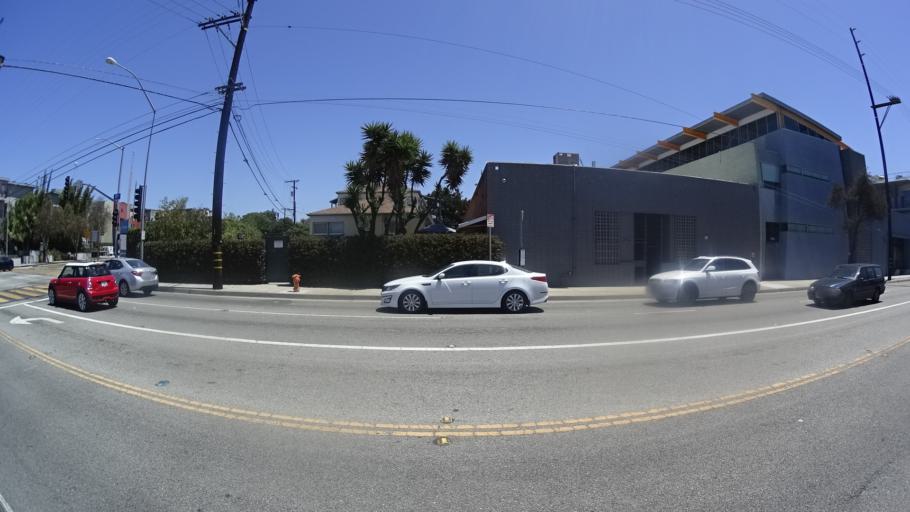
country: US
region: California
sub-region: Los Angeles County
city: Santa Monica
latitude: 34.0241
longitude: -118.4748
